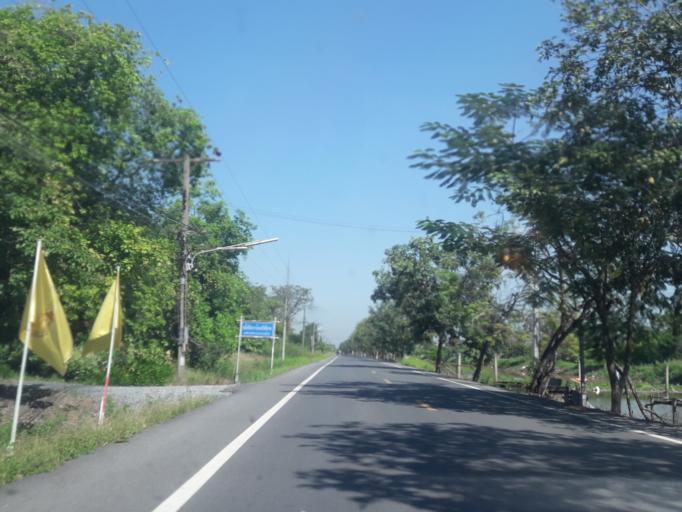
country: TH
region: Pathum Thani
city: Nong Suea
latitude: 14.1565
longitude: 100.8459
